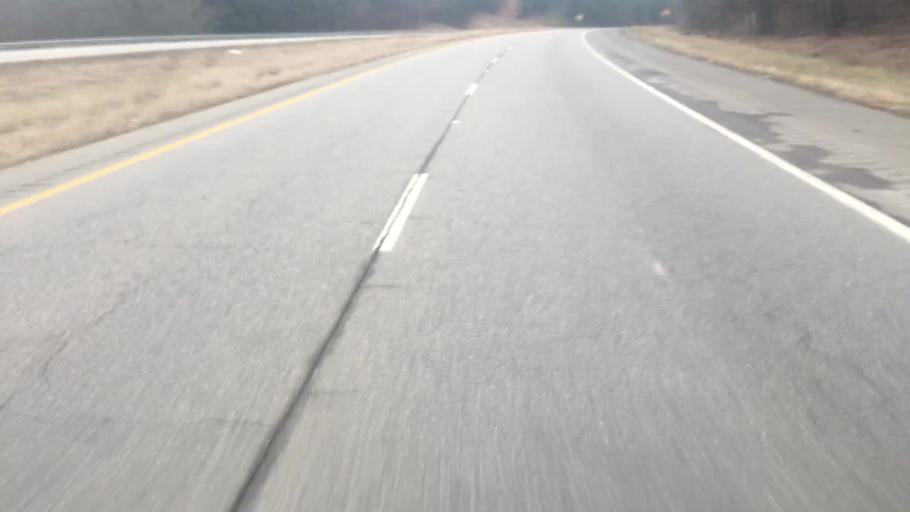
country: US
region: Alabama
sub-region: Walker County
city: Sumiton
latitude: 33.7732
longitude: -87.0740
